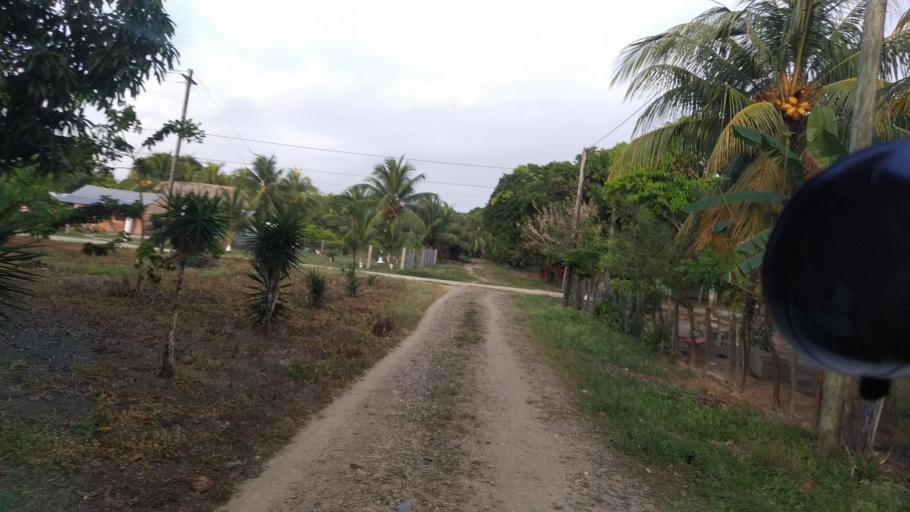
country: BZ
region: Stann Creek
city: Placencia
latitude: 16.5699
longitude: -88.5274
